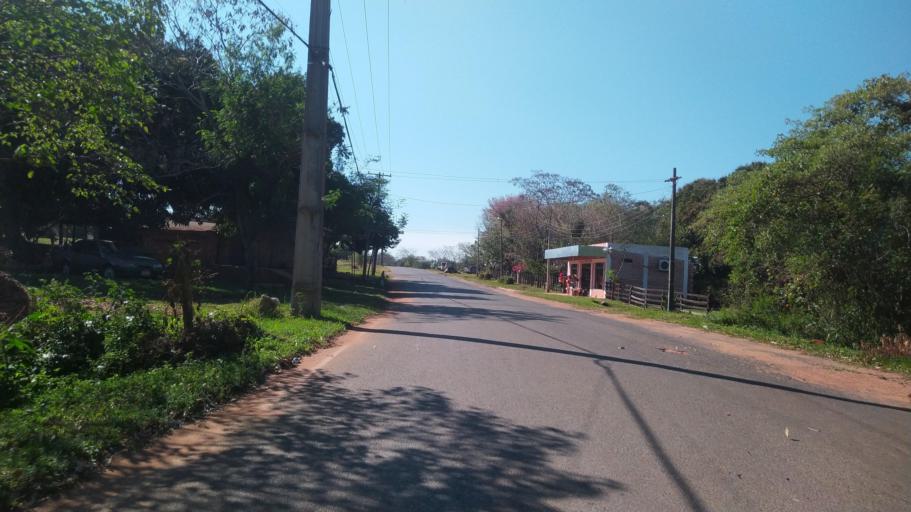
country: PY
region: Misiones
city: San Juan Bautista
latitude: -26.6744
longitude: -57.1367
